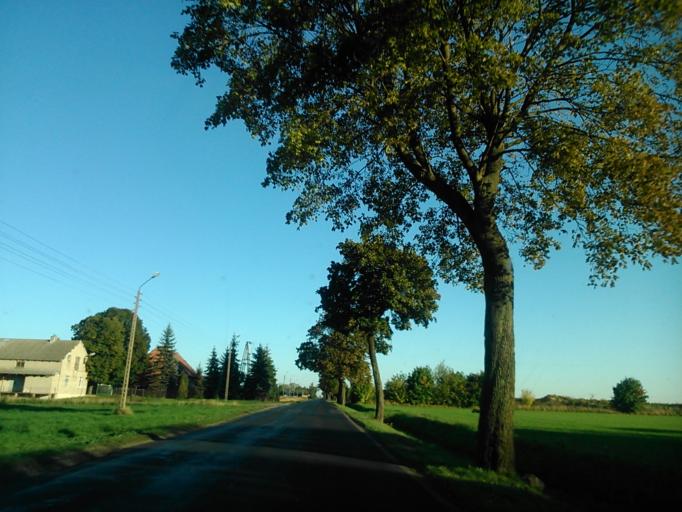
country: PL
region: Kujawsko-Pomorskie
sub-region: Powiat golubsko-dobrzynski
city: Golub-Dobrzyn
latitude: 53.1270
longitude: 19.0291
